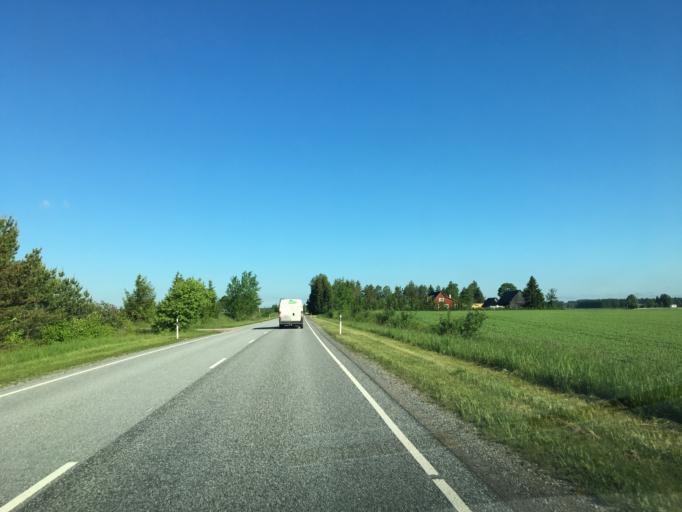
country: EE
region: Jogevamaa
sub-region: Tabivere vald
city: Tabivere
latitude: 58.4665
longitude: 26.6253
